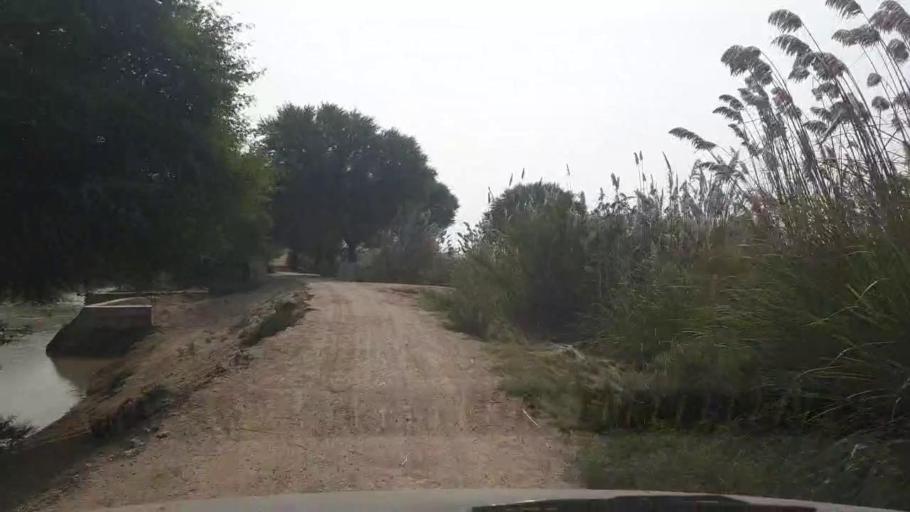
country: PK
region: Sindh
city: Tando Muhammad Khan
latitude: 25.1227
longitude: 68.4377
